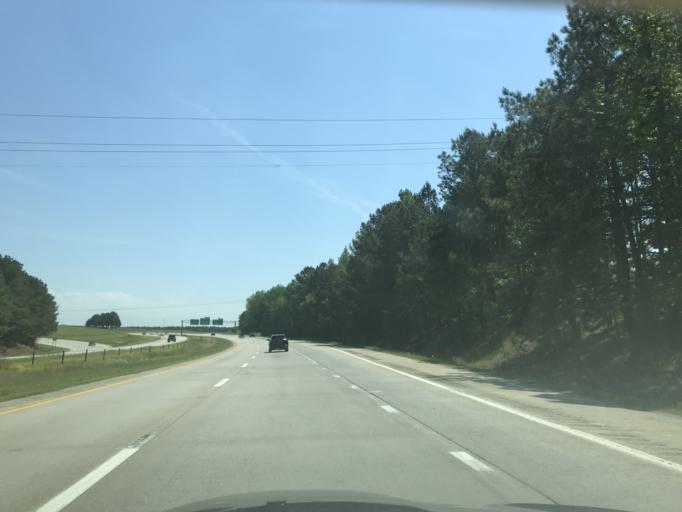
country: US
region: North Carolina
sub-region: Johnston County
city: Benson
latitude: 35.3976
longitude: -78.5227
